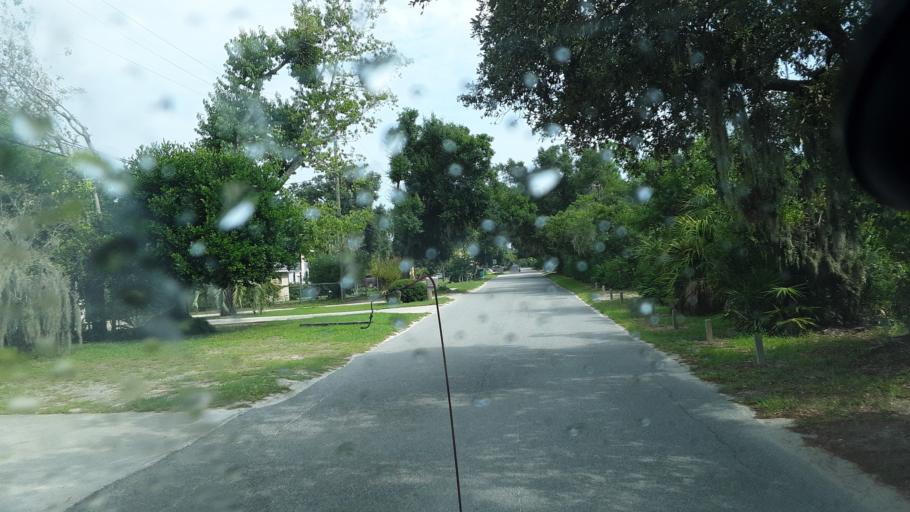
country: US
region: Georgia
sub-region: Chatham County
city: Tybee Island
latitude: 32.0133
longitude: -80.8676
